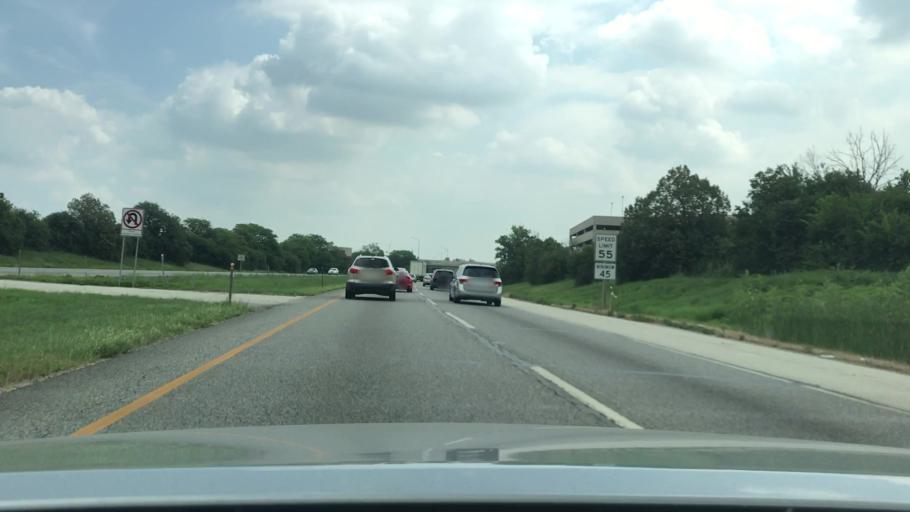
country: US
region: Illinois
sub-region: DuPage County
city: Oak Brook
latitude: 41.8509
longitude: -87.9250
